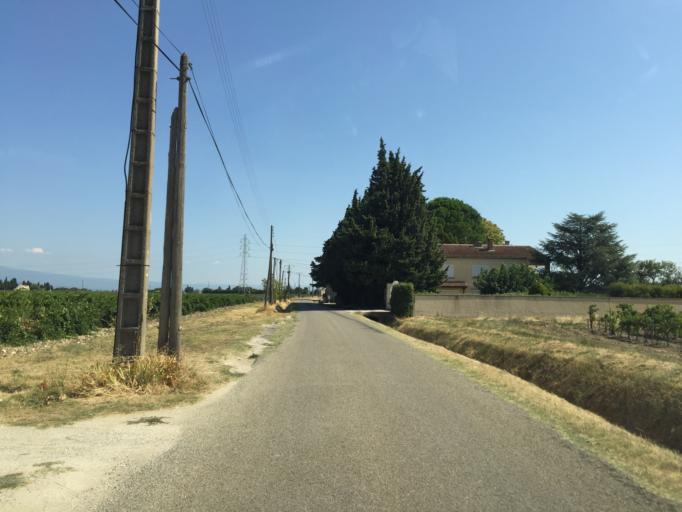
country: FR
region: Provence-Alpes-Cote d'Azur
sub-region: Departement du Vaucluse
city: Orange
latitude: 44.1052
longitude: 4.8277
